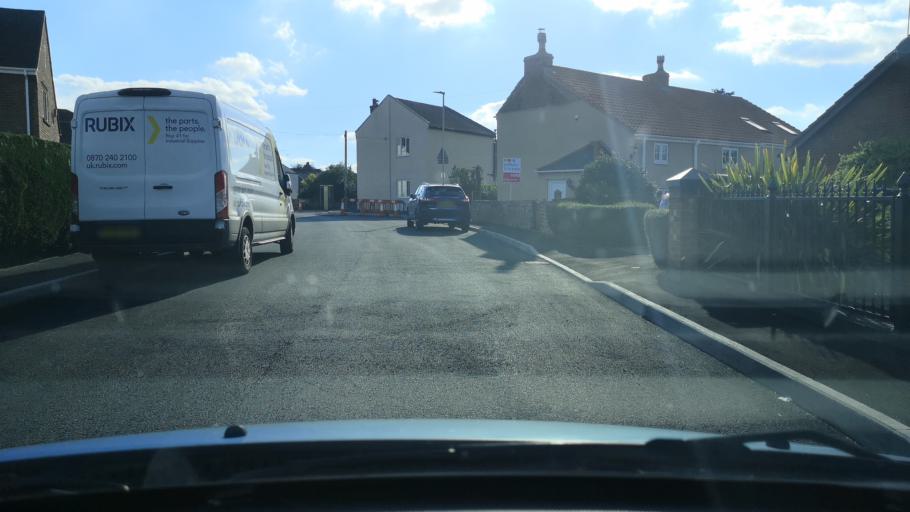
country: GB
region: England
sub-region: North Lincolnshire
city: Gunness
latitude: 53.5780
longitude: -0.7401
